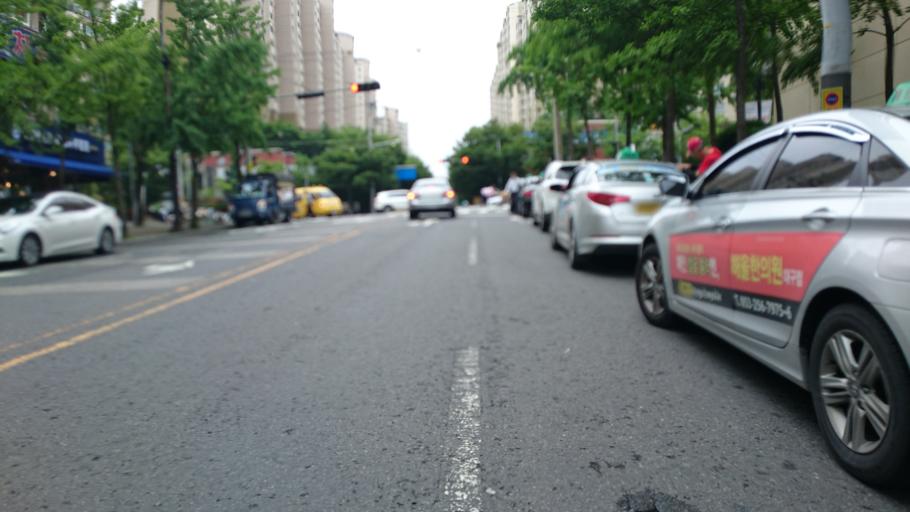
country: KR
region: Daegu
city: Daegu
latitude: 35.8705
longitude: 128.6372
